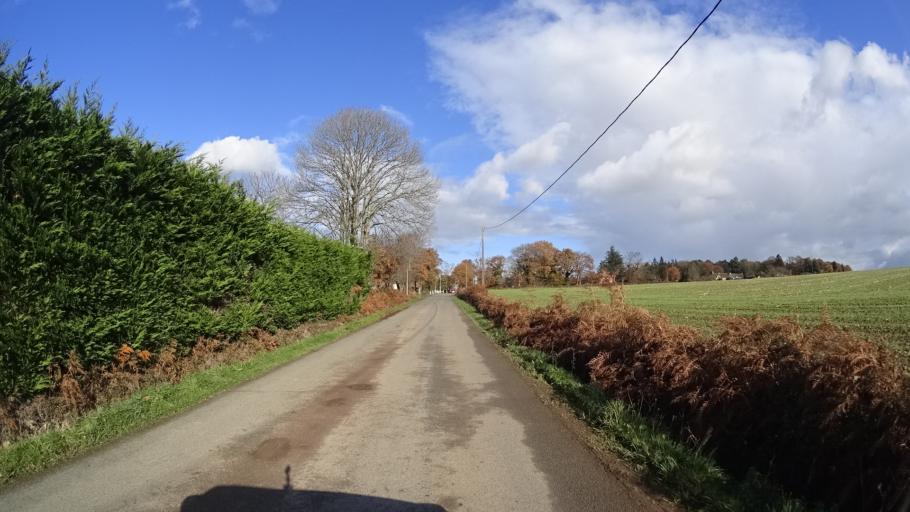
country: FR
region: Brittany
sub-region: Departement du Morbihan
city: Carentoir
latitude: 47.7921
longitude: -2.1507
